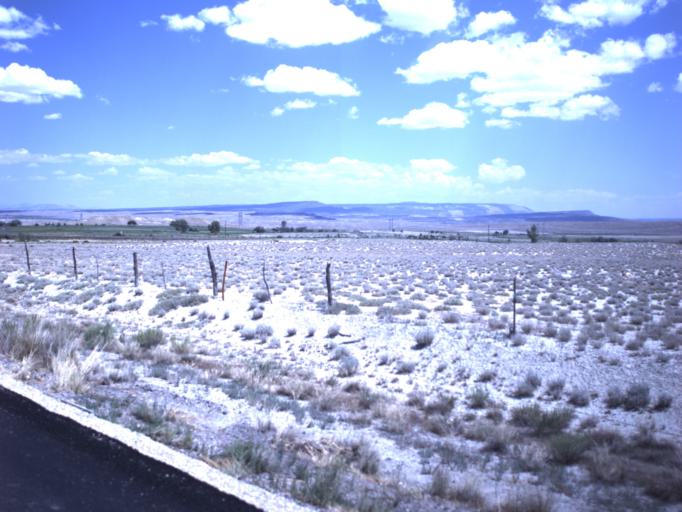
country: US
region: Utah
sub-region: Emery County
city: Castle Dale
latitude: 39.2434
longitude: -110.9939
